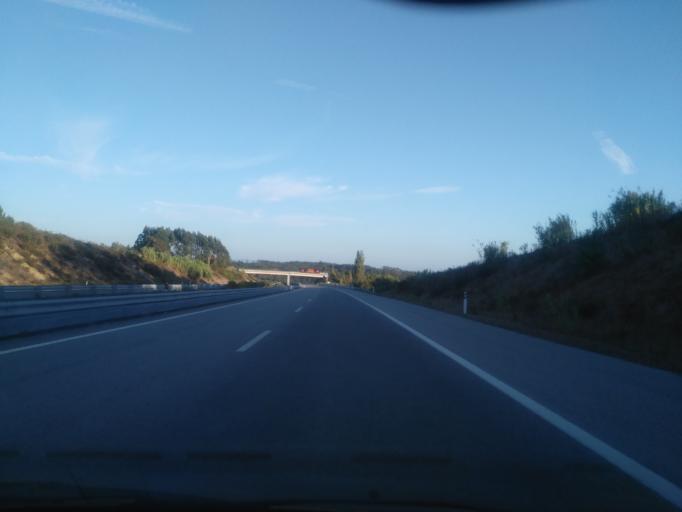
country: PT
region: Coimbra
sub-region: Figueira da Foz
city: Alhadas
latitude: 40.1835
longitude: -8.8082
